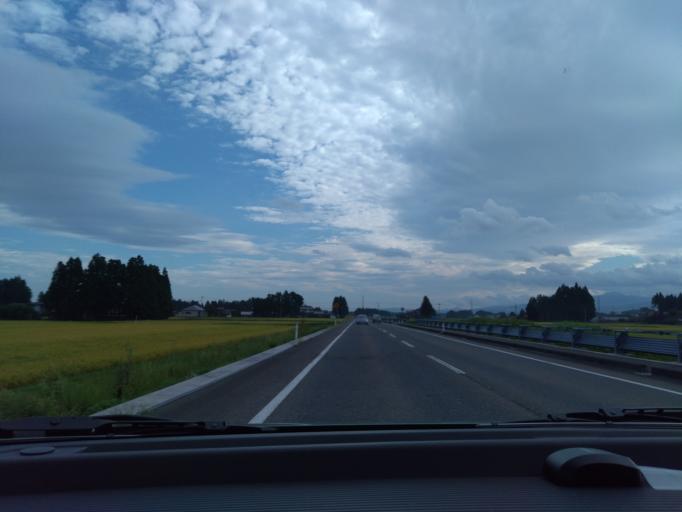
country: JP
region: Iwate
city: Hanamaki
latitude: 39.3515
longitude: 141.0535
